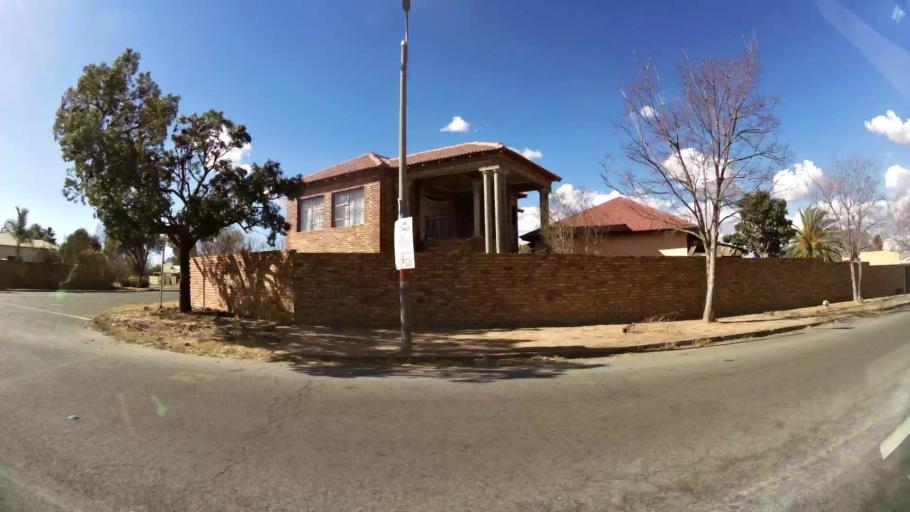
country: ZA
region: North-West
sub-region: Dr Kenneth Kaunda District Municipality
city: Klerksdorp
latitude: -26.8605
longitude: 26.6470
